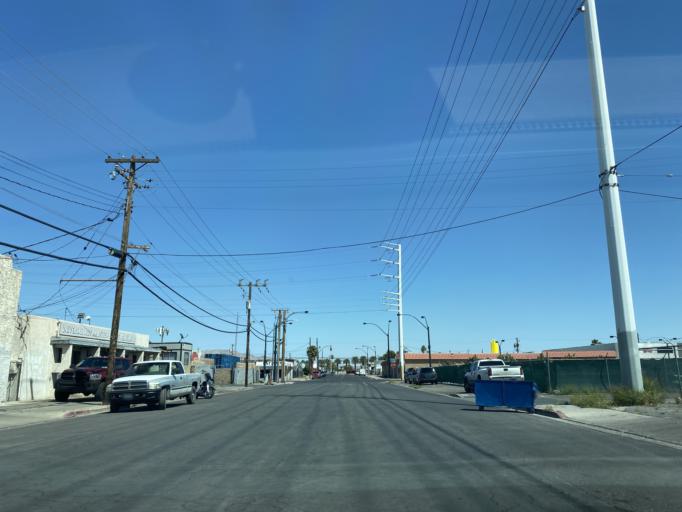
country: US
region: Nevada
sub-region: Clark County
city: Las Vegas
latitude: 36.1536
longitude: -115.1565
